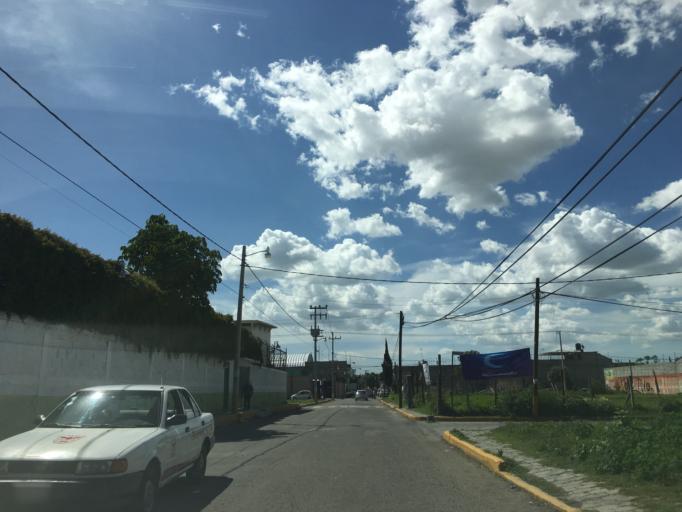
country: MX
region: Mexico
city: Ecatepec
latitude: 19.6137
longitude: -99.0542
